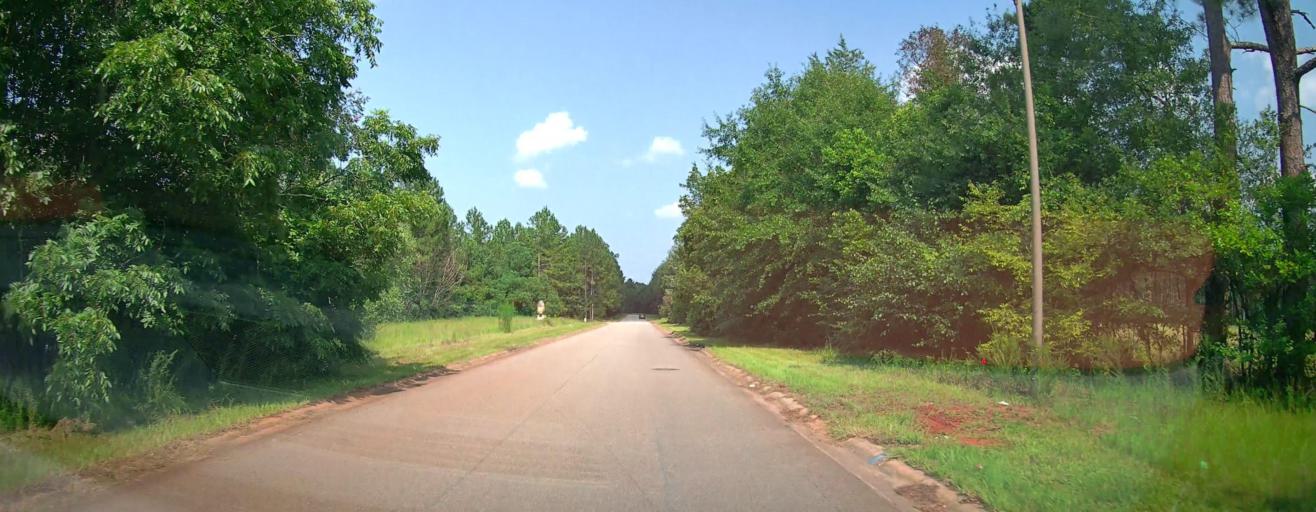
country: US
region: Georgia
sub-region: Houston County
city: Centerville
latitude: 32.6503
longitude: -83.7049
